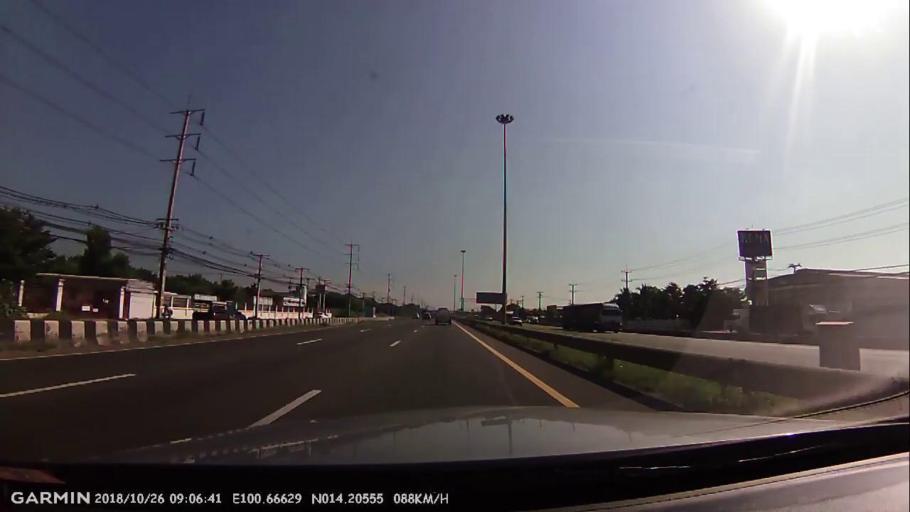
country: TH
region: Phra Nakhon Si Ayutthaya
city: Wang Noi
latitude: 14.2057
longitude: 100.6659
